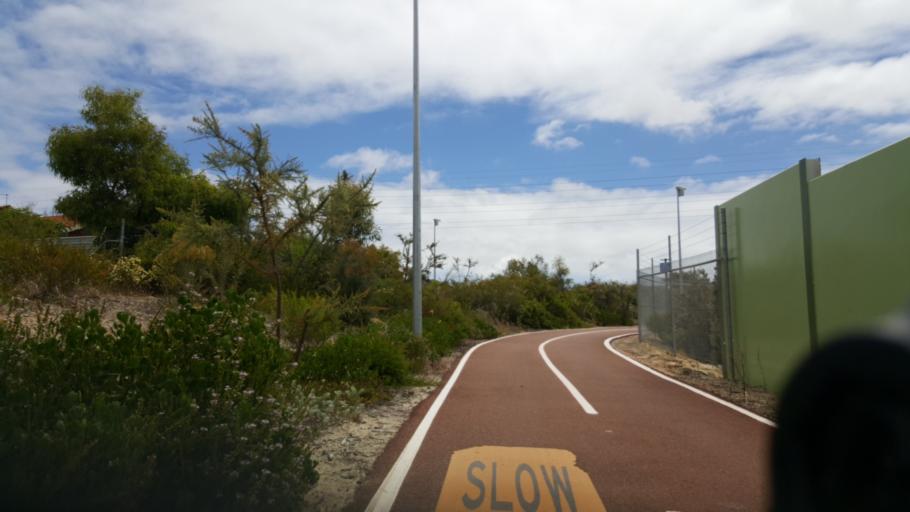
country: AU
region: Western Australia
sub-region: Bayswater
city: Embleton
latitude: -31.8686
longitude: 115.8896
